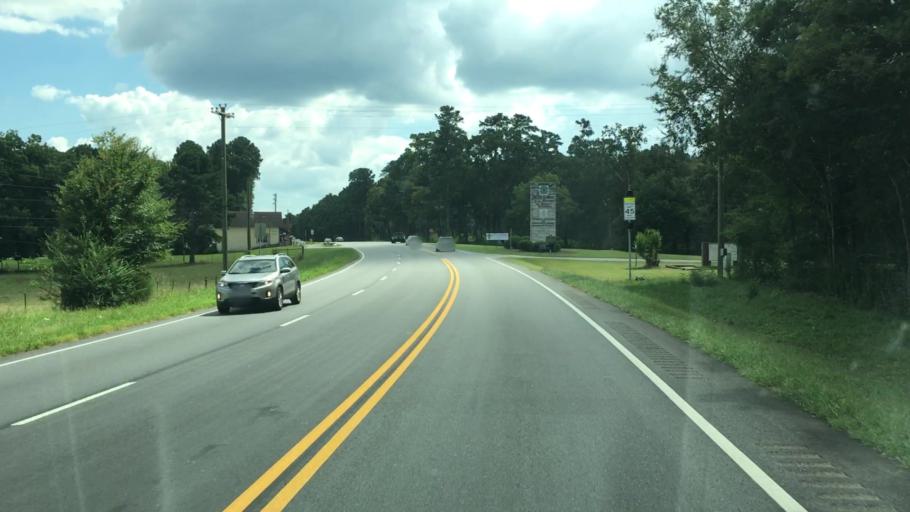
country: US
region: Georgia
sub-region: Putnam County
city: Jefferson
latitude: 33.4187
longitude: -83.3723
